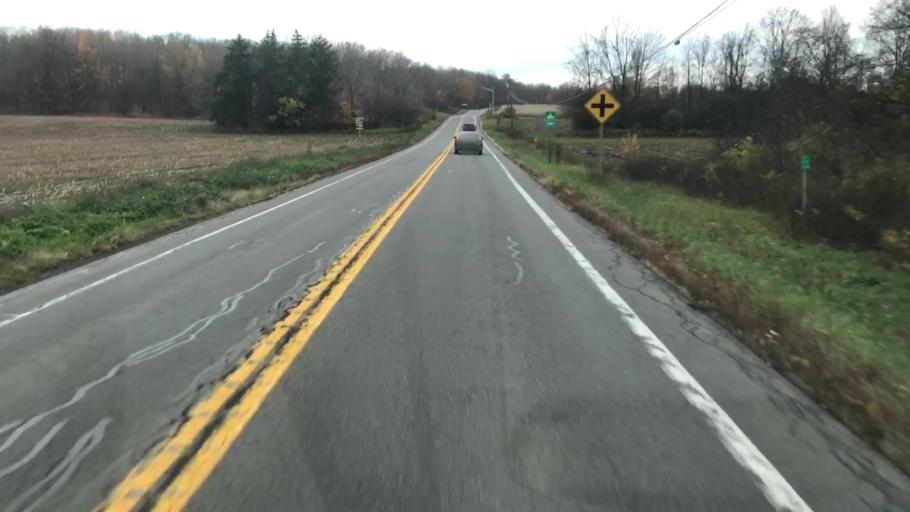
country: US
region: New York
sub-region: Onondaga County
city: Elbridge
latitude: 43.0119
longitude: -76.4108
